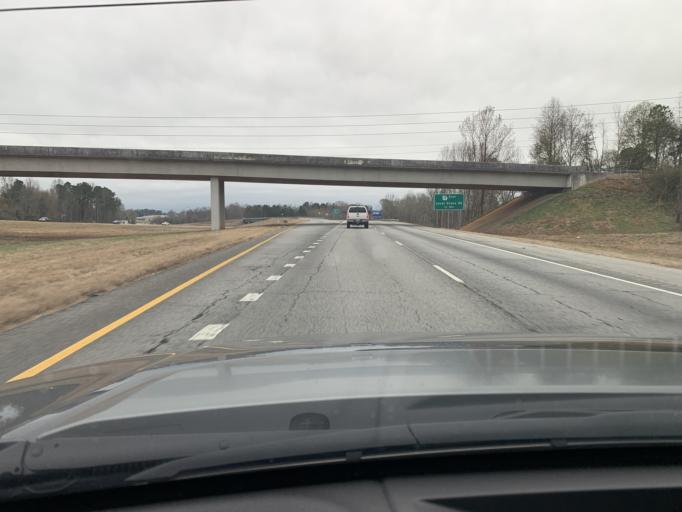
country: US
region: Georgia
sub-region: Habersham County
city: Cornelia
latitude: 34.5233
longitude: -83.5426
